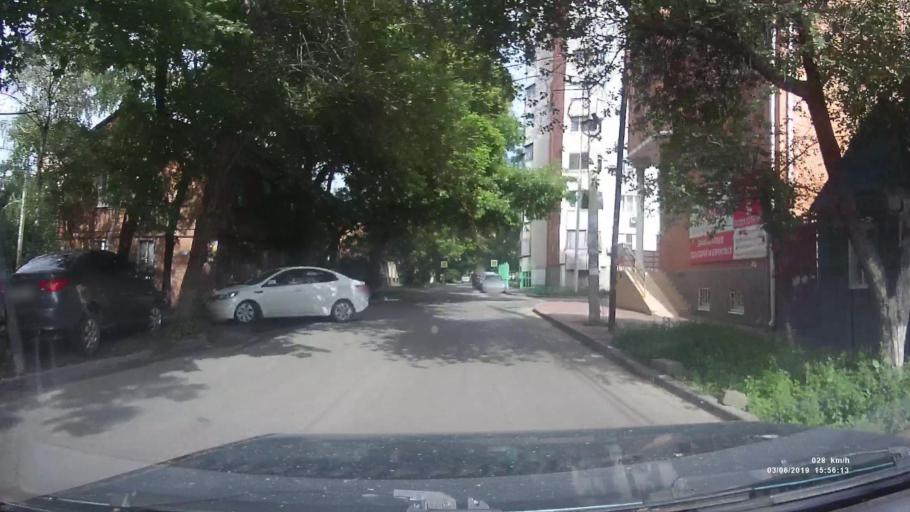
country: RU
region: Rostov
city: Rostov-na-Donu
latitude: 47.2455
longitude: 39.7149
